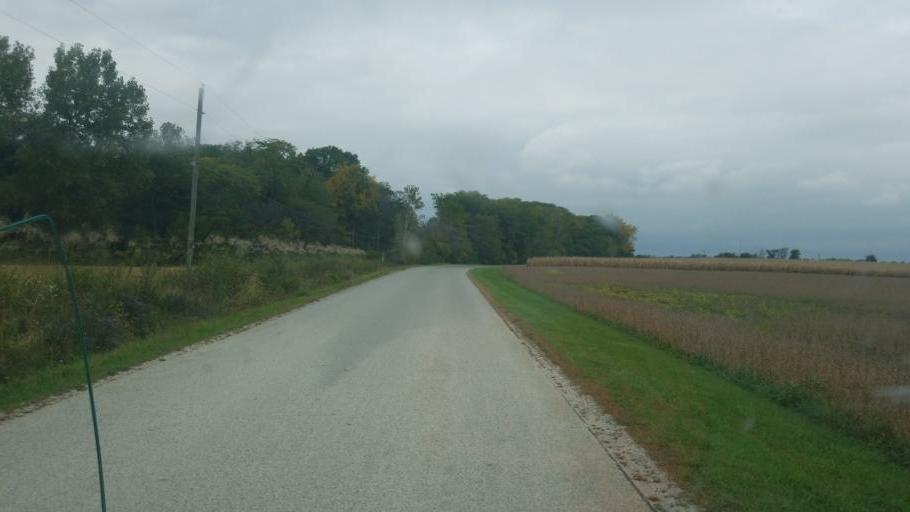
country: US
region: Ohio
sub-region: Wood County
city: Bowling Green
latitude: 41.3077
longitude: -83.6697
